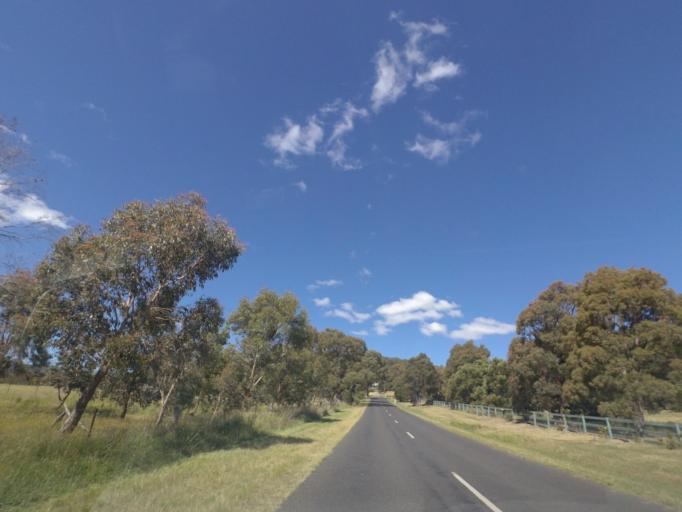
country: AU
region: Victoria
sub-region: Hume
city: Sunbury
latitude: -37.4290
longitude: 144.6141
